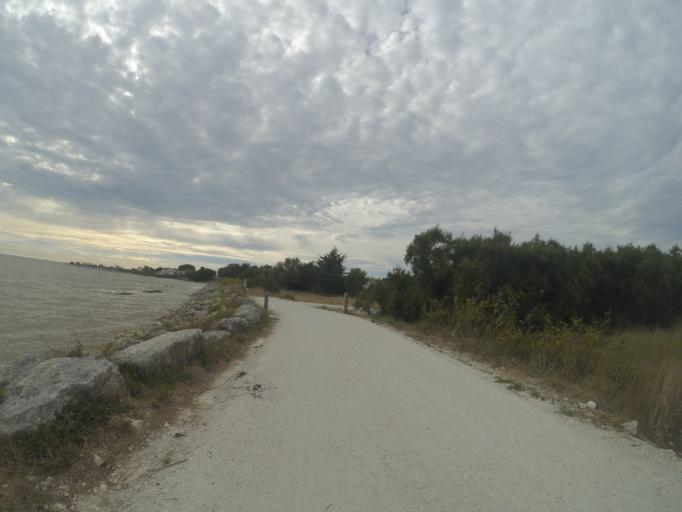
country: FR
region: Poitou-Charentes
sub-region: Departement de la Charente-Maritime
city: Meschers-sur-Gironde
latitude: 45.5511
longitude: -0.9180
